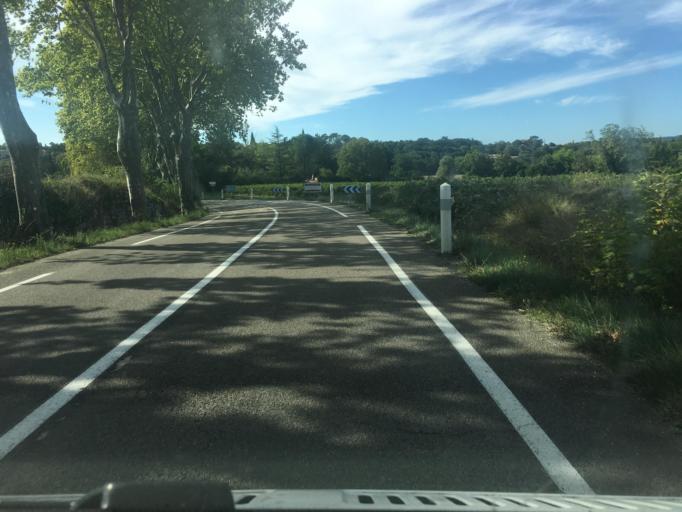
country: FR
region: Languedoc-Roussillon
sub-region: Departement du Gard
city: Saint-Quentin-la-Poterie
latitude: 44.0212
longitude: 4.4392
